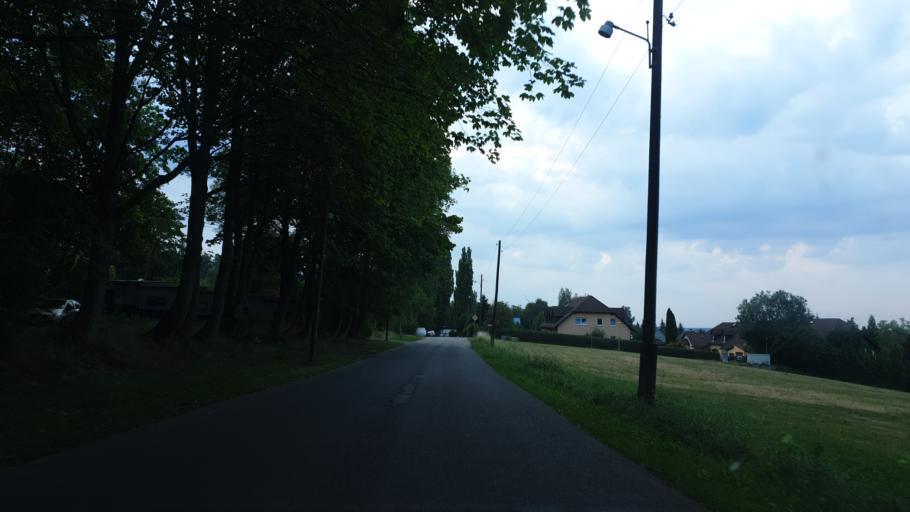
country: DE
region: Saxony
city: Lugau
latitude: 50.7358
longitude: 12.7313
